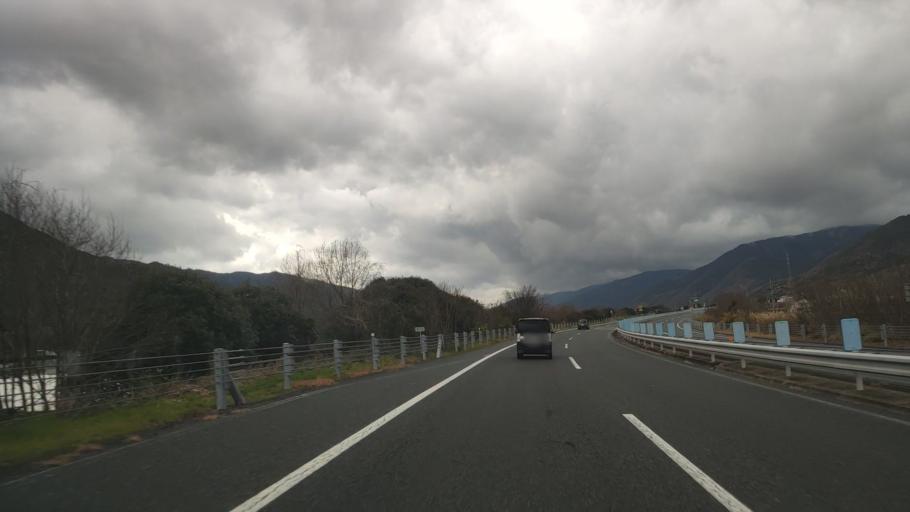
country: JP
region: Tokushima
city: Ikedacho
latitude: 34.0367
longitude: 133.9020
